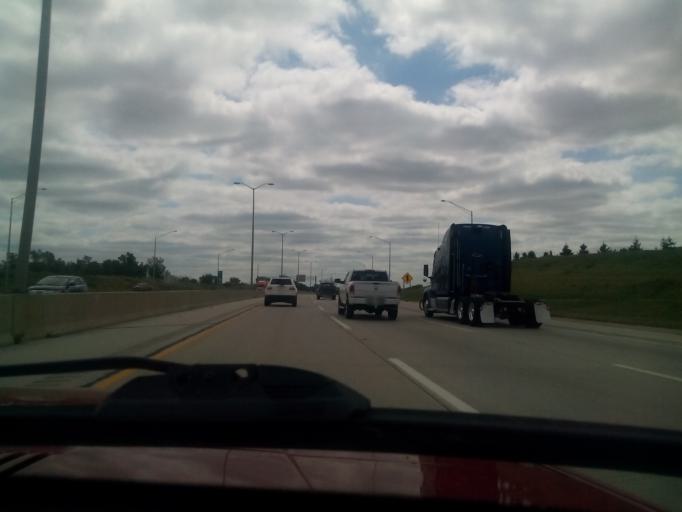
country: US
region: Illinois
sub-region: Cook County
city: Lemont
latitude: 41.6548
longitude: -88.0171
